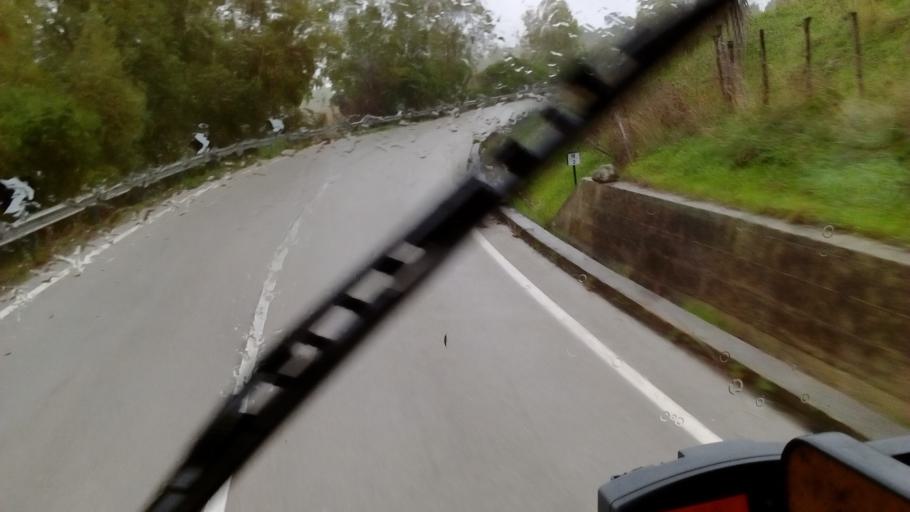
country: IT
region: Sicily
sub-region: Enna
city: Pietraperzia
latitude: 37.4758
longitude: 14.1637
